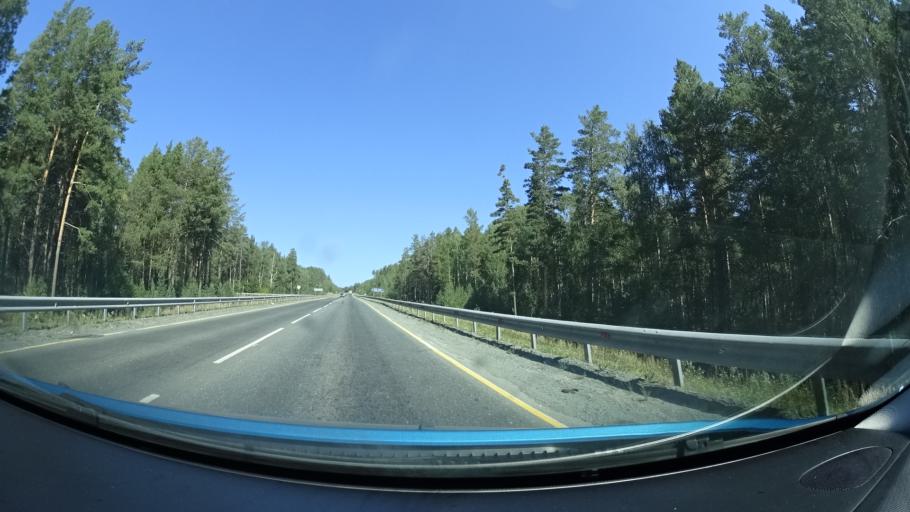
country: RU
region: Bashkortostan
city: Abzakovo
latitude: 53.8796
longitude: 58.5319
